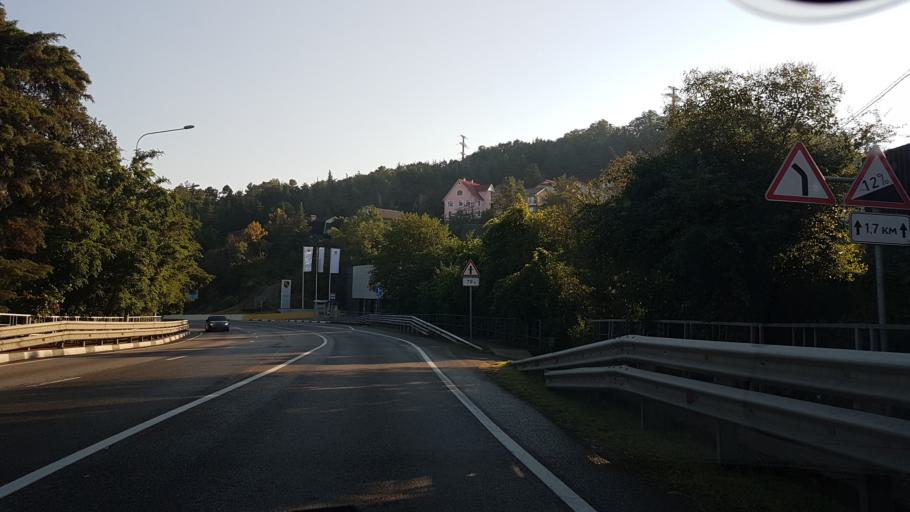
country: RU
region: Krasnodarskiy
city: Dagomys
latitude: 43.6558
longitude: 39.6923
